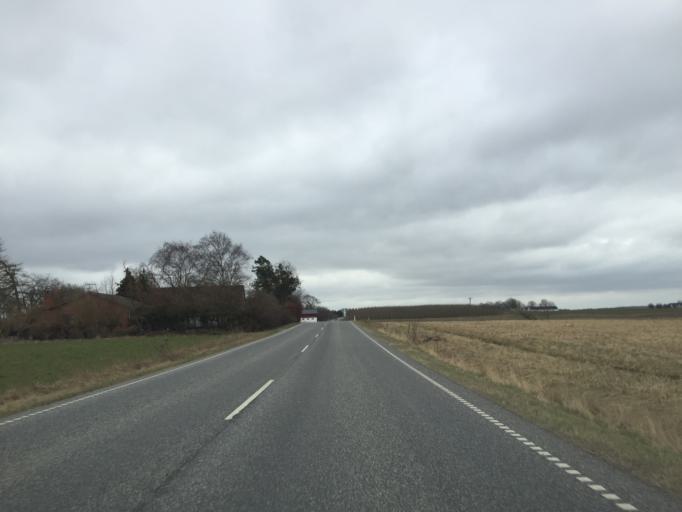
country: DK
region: Capital Region
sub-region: Allerod Kommune
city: Lynge
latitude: 55.8766
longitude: 12.2728
